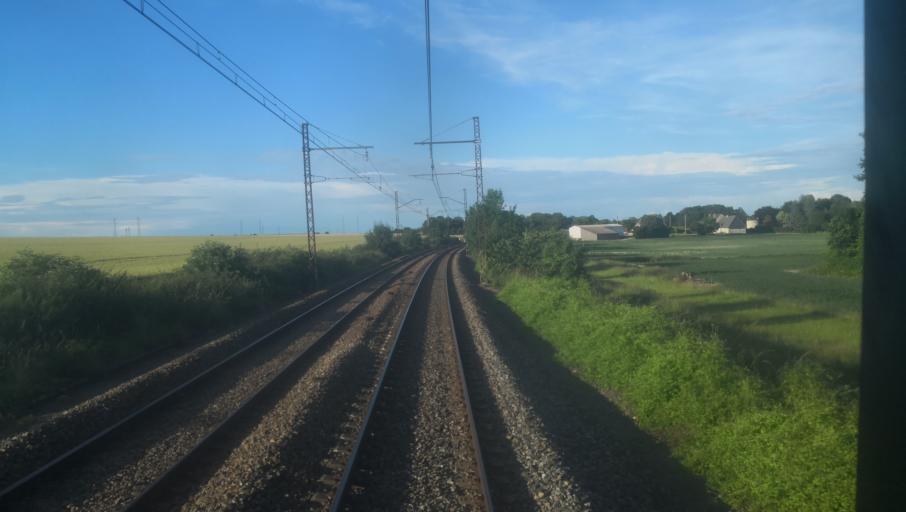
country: FR
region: Centre
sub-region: Departement de l'Indre
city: Issoudun
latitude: 46.9223
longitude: 1.9484
